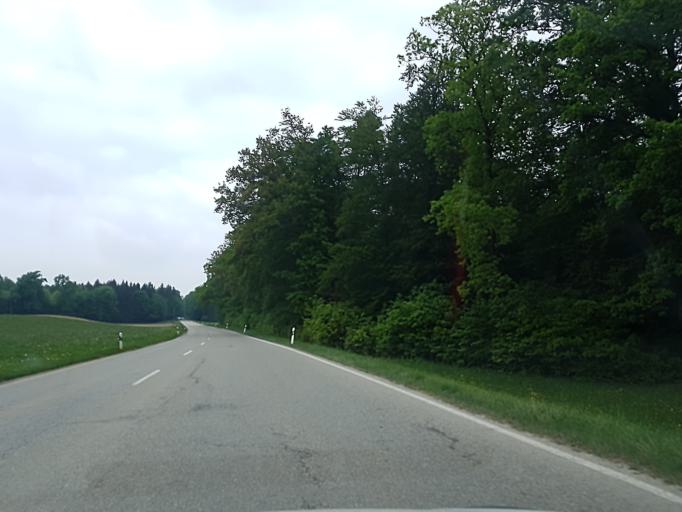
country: DE
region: Bavaria
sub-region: Upper Bavaria
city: Ebersberg
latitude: 48.1022
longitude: 11.9803
